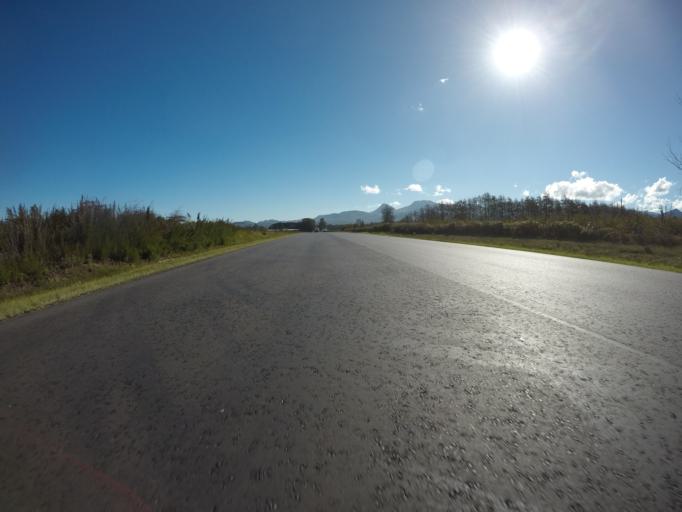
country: ZA
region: Western Cape
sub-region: Overberg District Municipality
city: Grabouw
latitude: -34.1741
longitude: 19.0536
